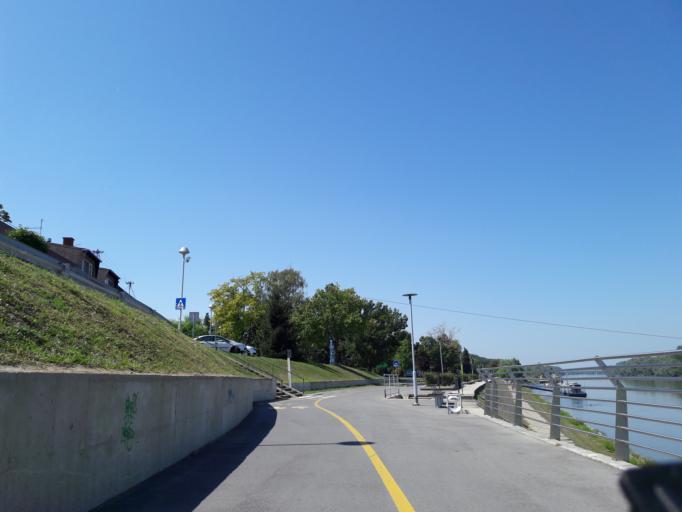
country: HR
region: Osjecko-Baranjska
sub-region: Grad Osijek
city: Osijek
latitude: 45.5659
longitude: 18.6690
